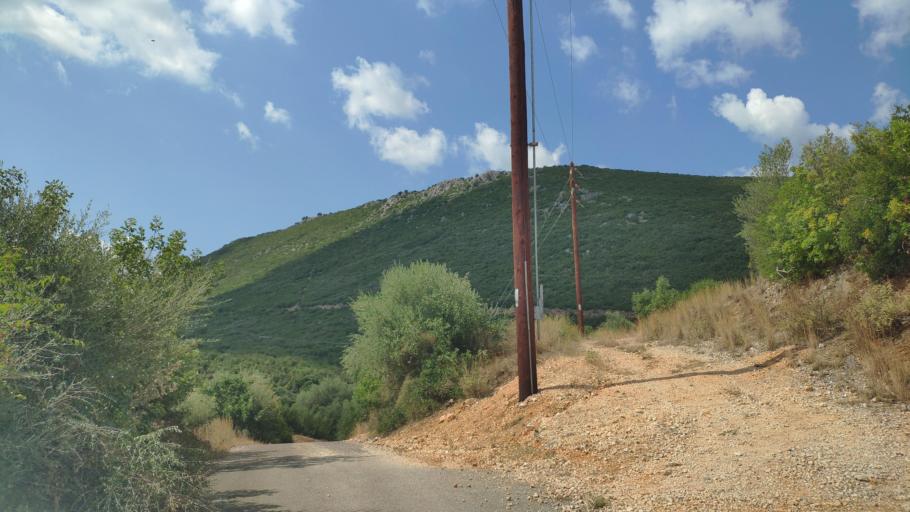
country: GR
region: West Greece
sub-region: Nomos Aitolias kai Akarnanias
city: Fitiai
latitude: 38.6699
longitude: 21.1444
